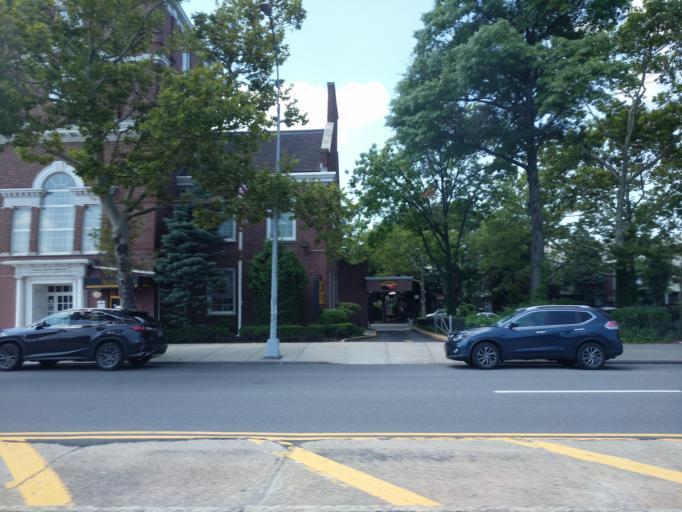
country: US
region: New York
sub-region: Queens County
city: Jamaica
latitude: 40.7230
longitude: -73.8198
